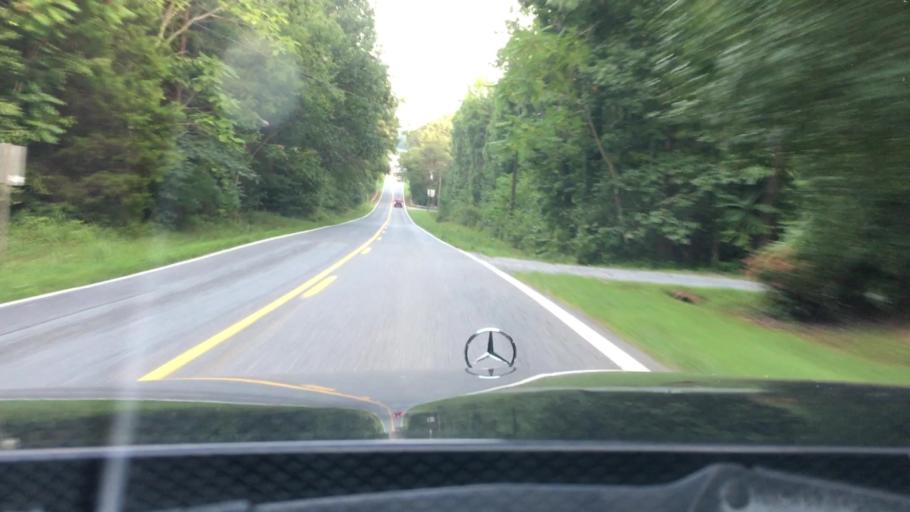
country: US
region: Virginia
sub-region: Campbell County
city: Altavista
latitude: 37.1404
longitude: -79.2945
